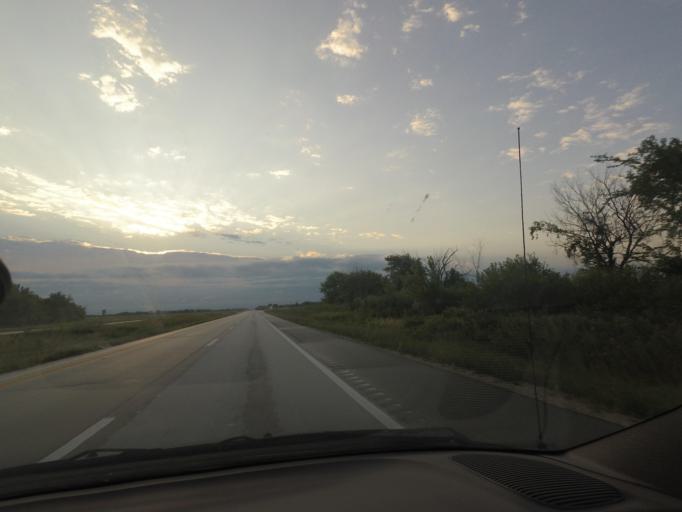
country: US
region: Missouri
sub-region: Shelby County
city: Shelbina
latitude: 39.7279
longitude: -92.1867
